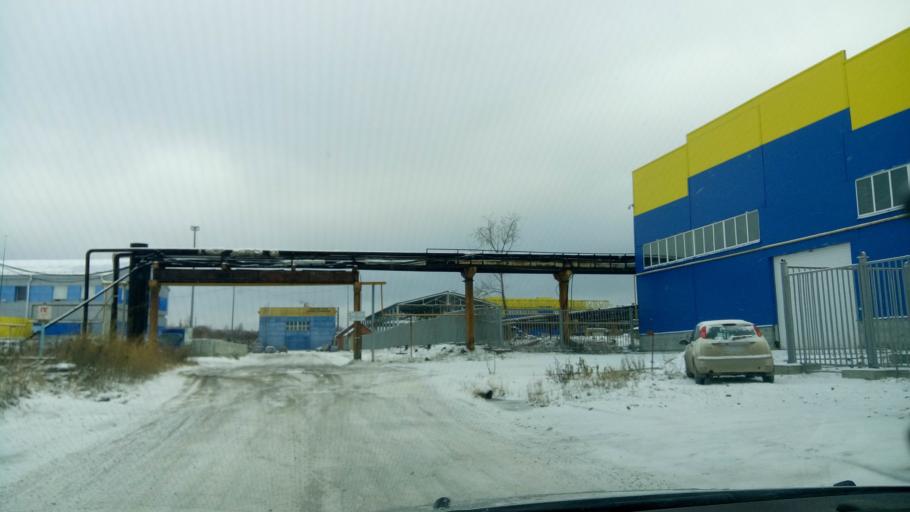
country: RU
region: Sverdlovsk
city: Polevskoy
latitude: 56.4704
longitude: 60.1759
